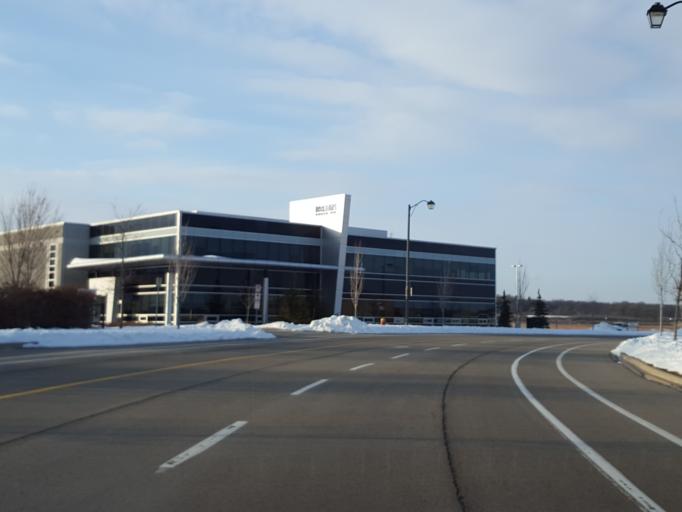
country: CA
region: Ontario
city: Burlington
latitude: 43.3989
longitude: -79.8297
